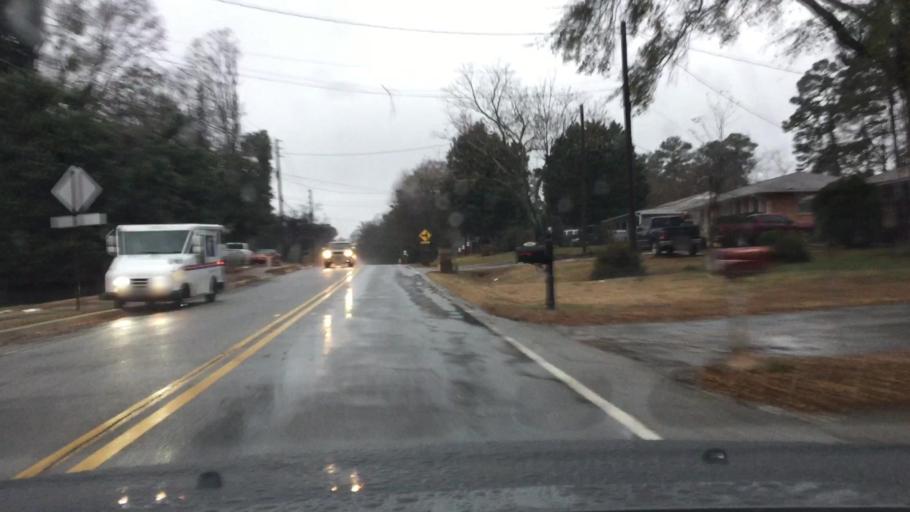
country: US
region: Georgia
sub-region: Cobb County
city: Fair Oaks
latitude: 33.9023
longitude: -84.5592
